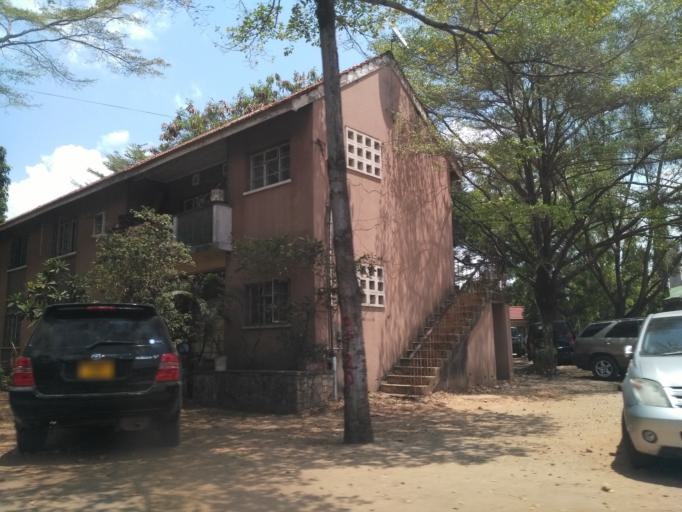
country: TZ
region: Dar es Salaam
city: Dar es Salaam
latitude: -6.8019
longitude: 39.2726
